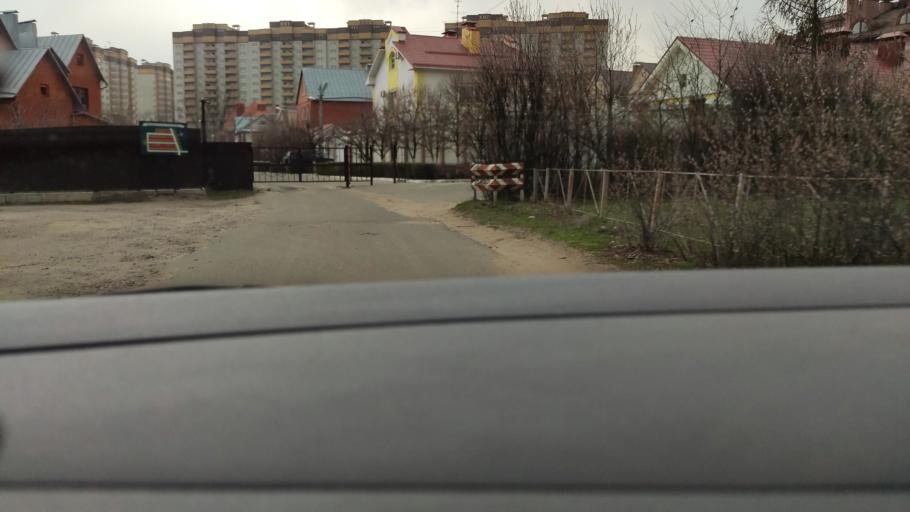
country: RU
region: Voronezj
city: Podgornoye
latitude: 51.7350
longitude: 39.1875
